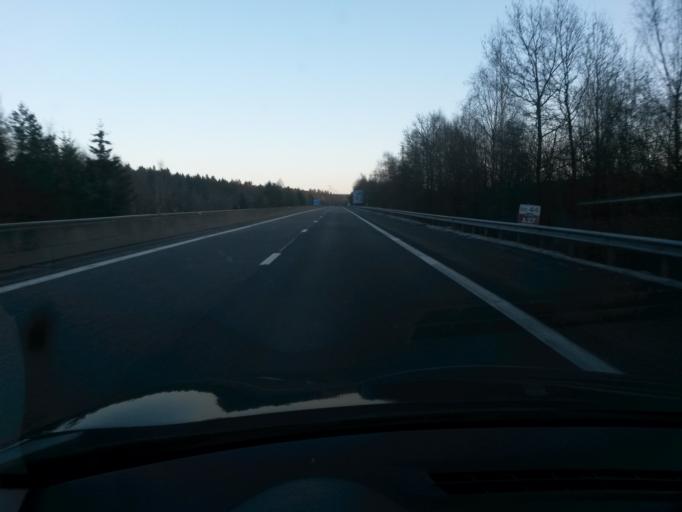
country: BE
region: Wallonia
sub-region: Province de Liege
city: Waimes
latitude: 50.3508
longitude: 6.0736
